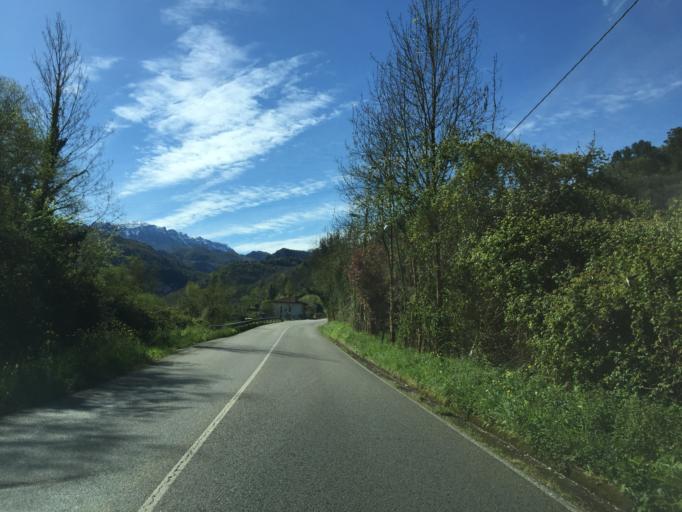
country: ES
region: Asturias
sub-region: Province of Asturias
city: Proaza
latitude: 43.3235
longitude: -5.9928
